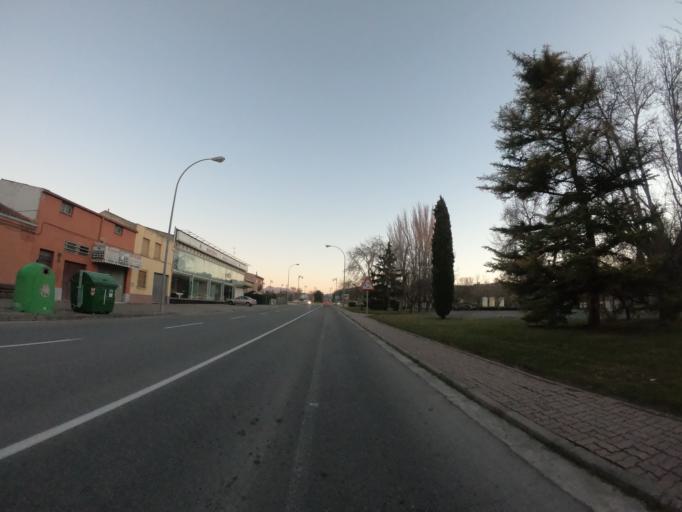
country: ES
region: La Rioja
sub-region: Provincia de La Rioja
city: Logrono
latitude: 42.4745
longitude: -2.4447
